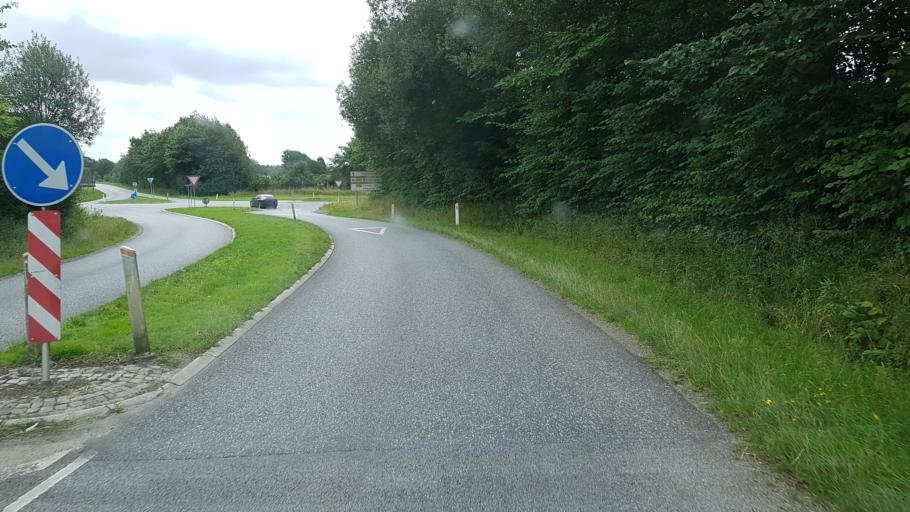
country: DK
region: South Denmark
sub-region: Kolding Kommune
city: Lunderskov
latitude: 55.4569
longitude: 9.3827
